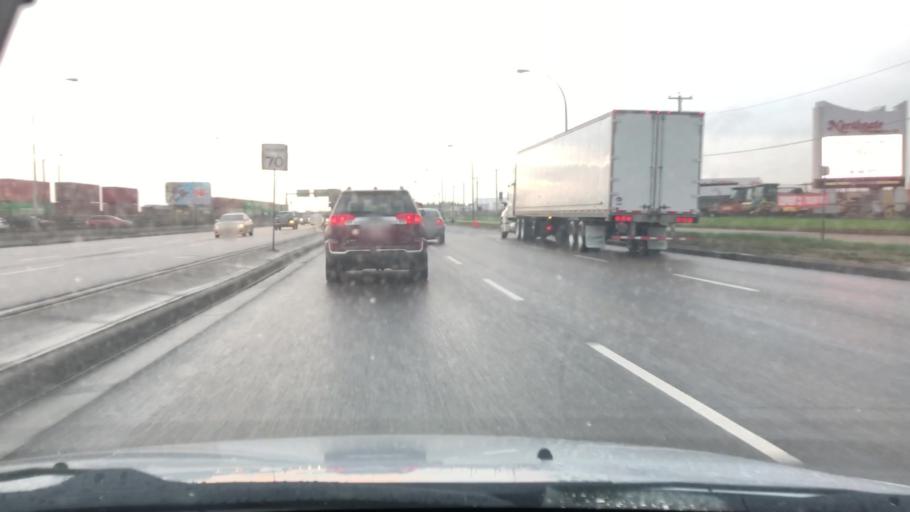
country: CA
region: Alberta
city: Edmonton
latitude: 53.5808
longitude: -113.5238
